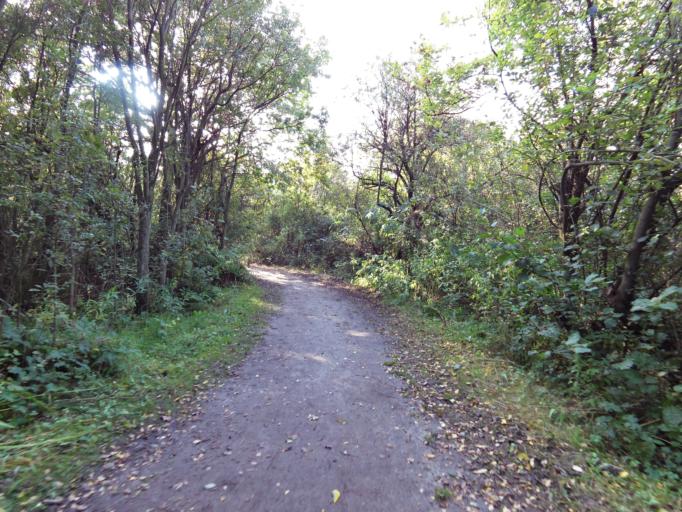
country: NL
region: South Holland
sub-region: Gemeente Hellevoetsluis
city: Nieuw-Helvoet
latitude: 51.8480
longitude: 4.0793
